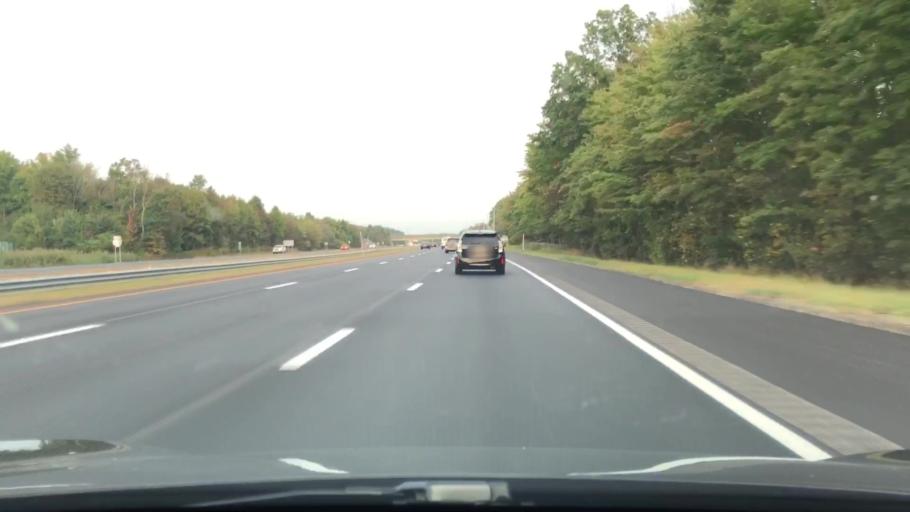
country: US
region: New Jersey
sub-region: Mercer County
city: Ewing
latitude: 40.2893
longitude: -74.7929
